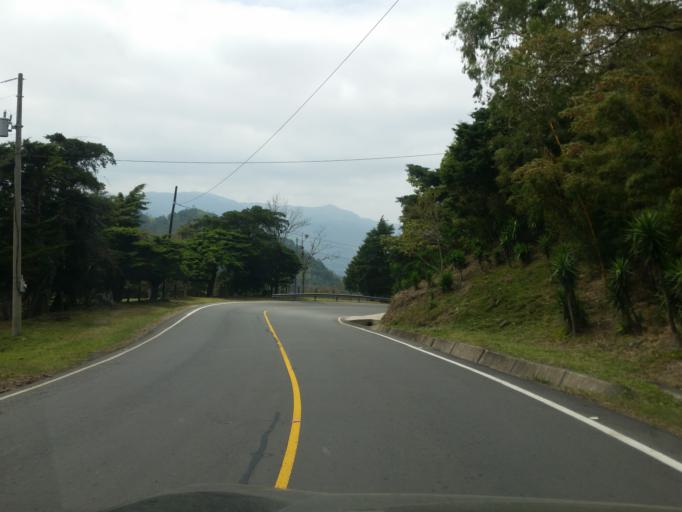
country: NI
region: Matagalpa
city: Matagalpa
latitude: 12.9814
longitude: -85.9214
